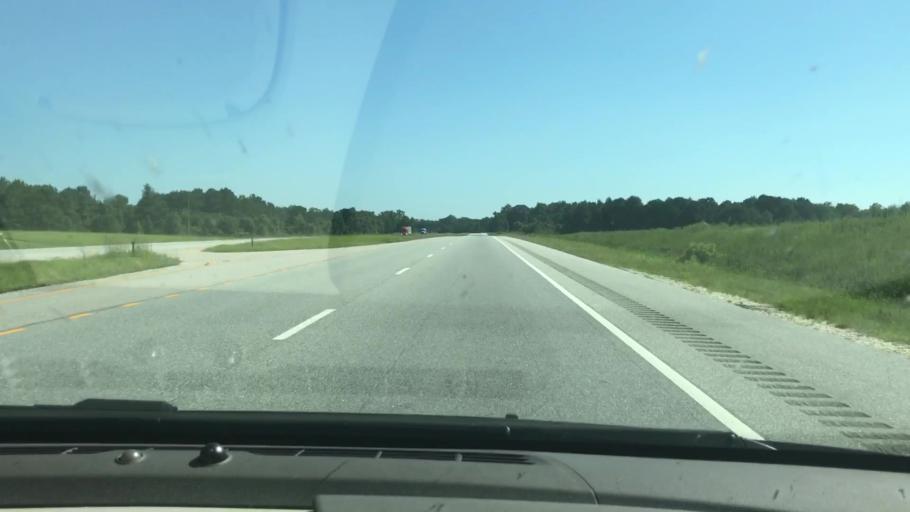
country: US
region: Alabama
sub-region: Russell County
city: Ladonia
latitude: 32.3613
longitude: -85.1041
